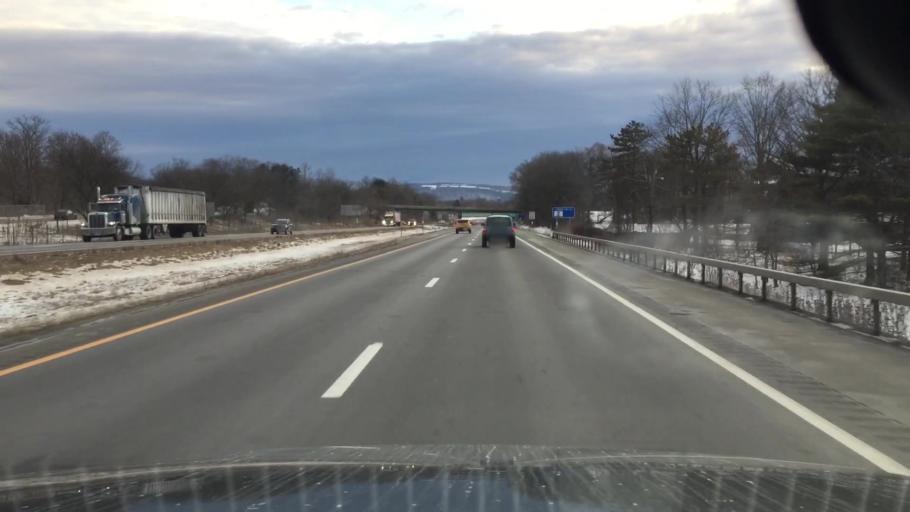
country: US
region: Pennsylvania
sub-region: Bradford County
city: South Waverly
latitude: 41.9989
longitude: -76.5392
